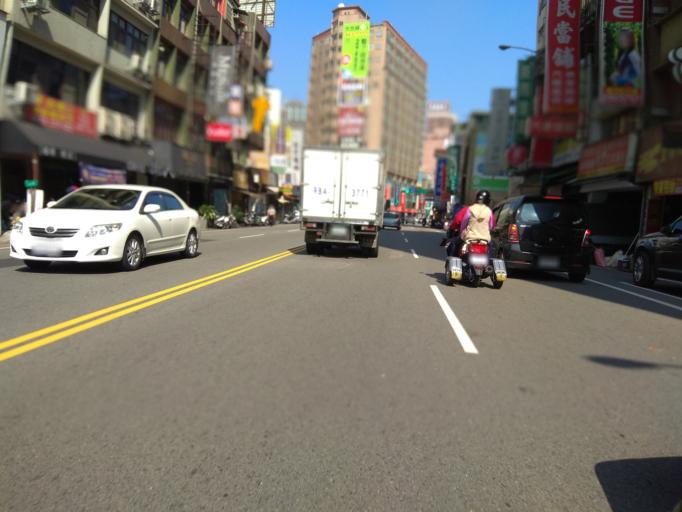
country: TW
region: Taiwan
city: Taoyuan City
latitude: 24.9584
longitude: 121.2242
